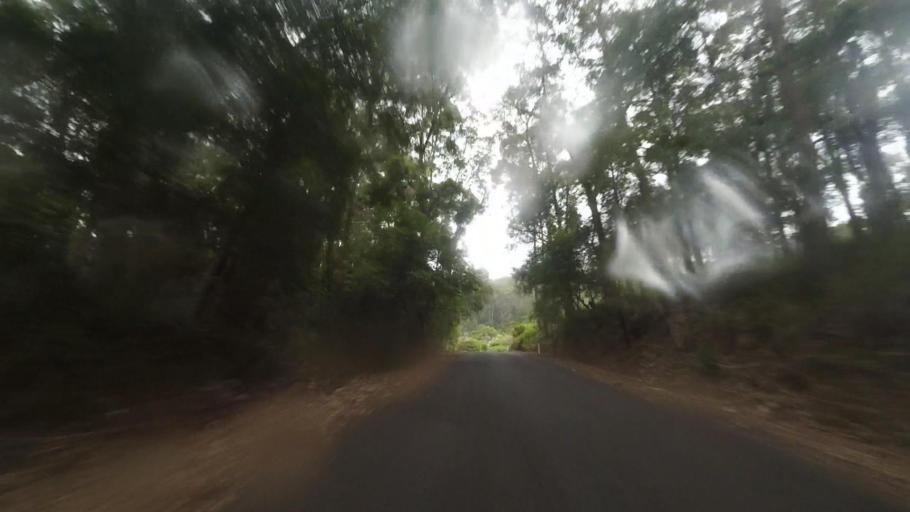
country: AU
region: New South Wales
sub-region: Wollongong
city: Cordeaux Heights
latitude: -34.4096
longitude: 150.8159
